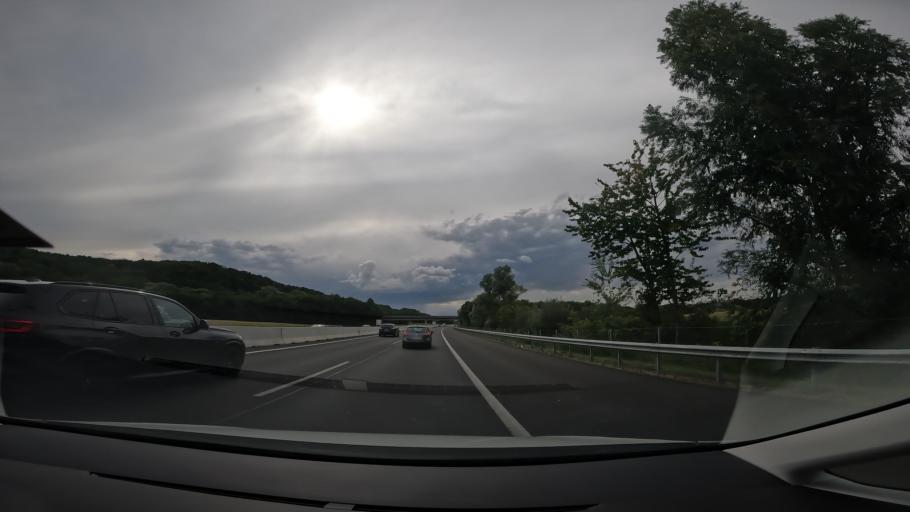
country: AT
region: Styria
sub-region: Politischer Bezirk Hartberg-Fuerstenfeld
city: Ilz
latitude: 47.0773
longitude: 15.9476
